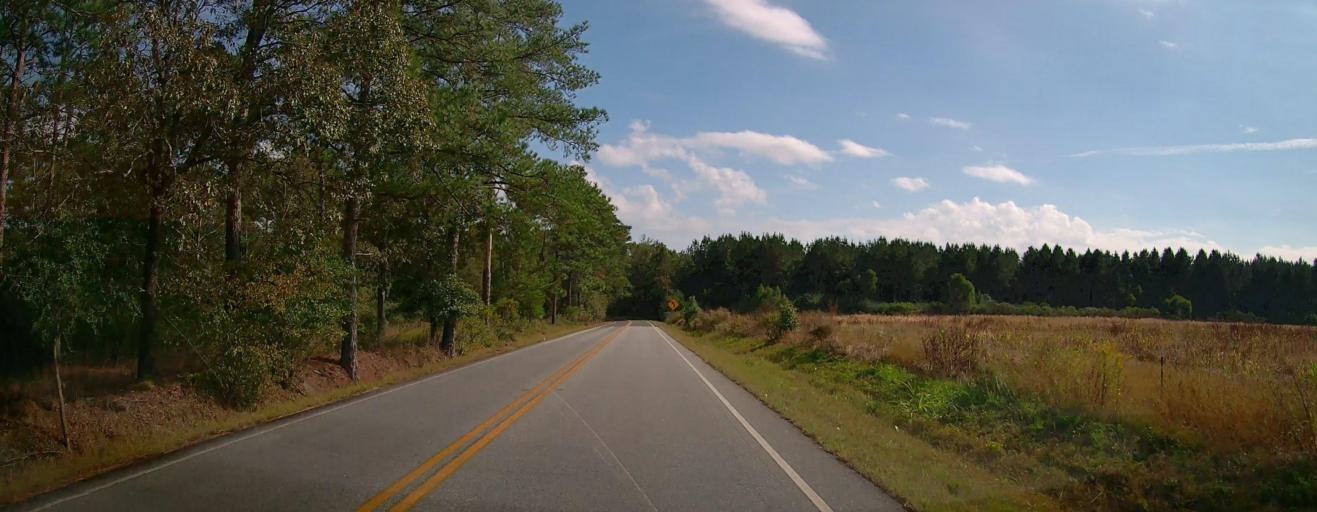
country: US
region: Georgia
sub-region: Thomas County
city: Thomasville
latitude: 30.9391
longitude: -84.0299
